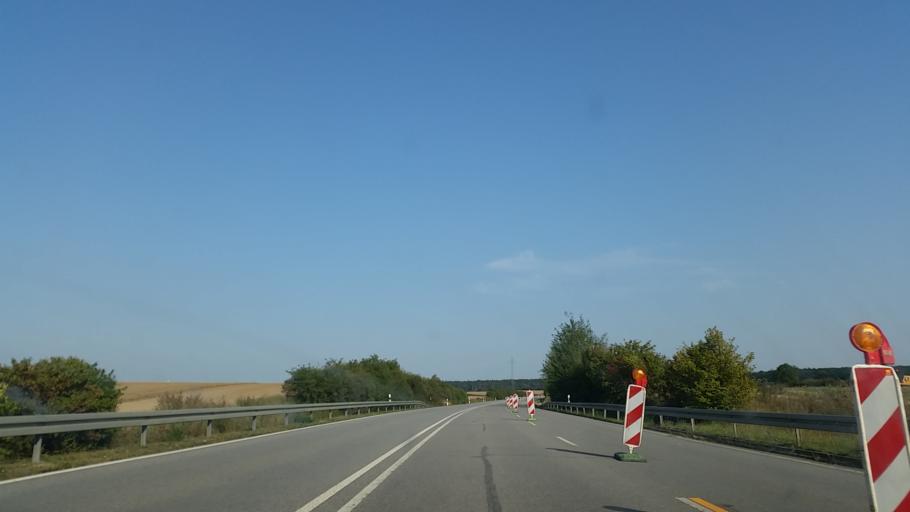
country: DE
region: Brandenburg
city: Pinnow
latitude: 53.0737
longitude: 14.1008
